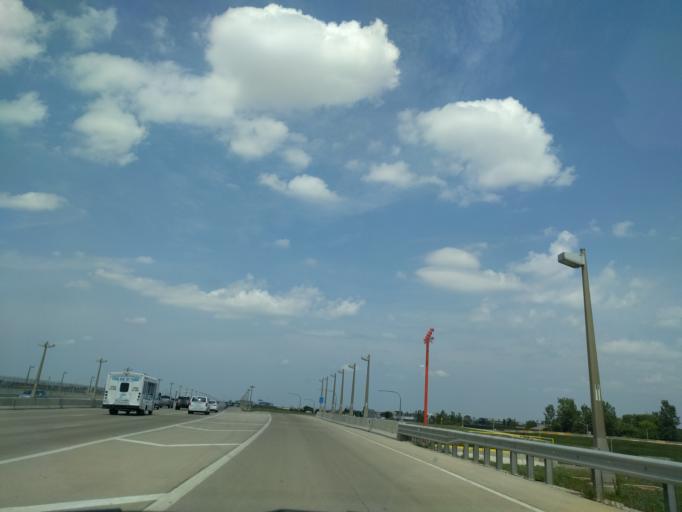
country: US
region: Illinois
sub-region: Cook County
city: Schiller Park
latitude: 41.9687
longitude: -87.8763
